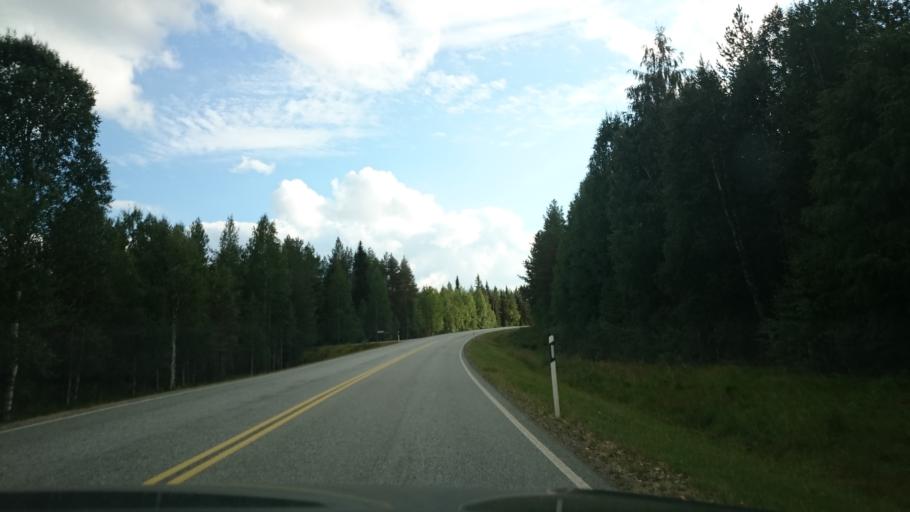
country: FI
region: Kainuu
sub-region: Kehys-Kainuu
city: Kuhmo
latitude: 64.5185
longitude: 29.9460
